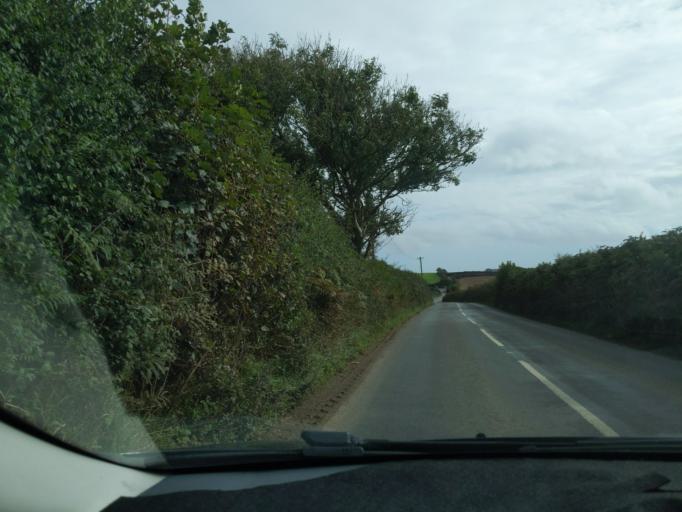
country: GB
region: England
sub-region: Cornwall
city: Mevagissey
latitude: 50.2529
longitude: -4.8223
